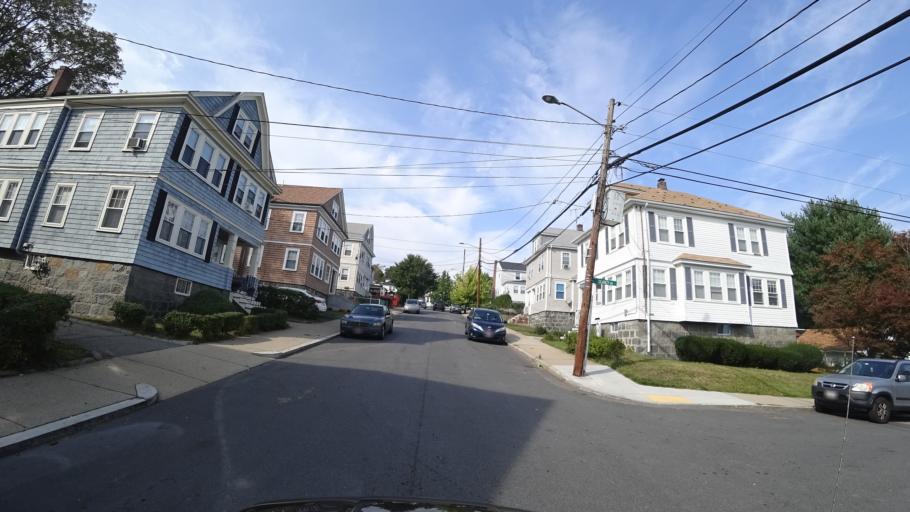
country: US
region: Massachusetts
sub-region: Norfolk County
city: Milton
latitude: 42.2774
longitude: -71.0726
